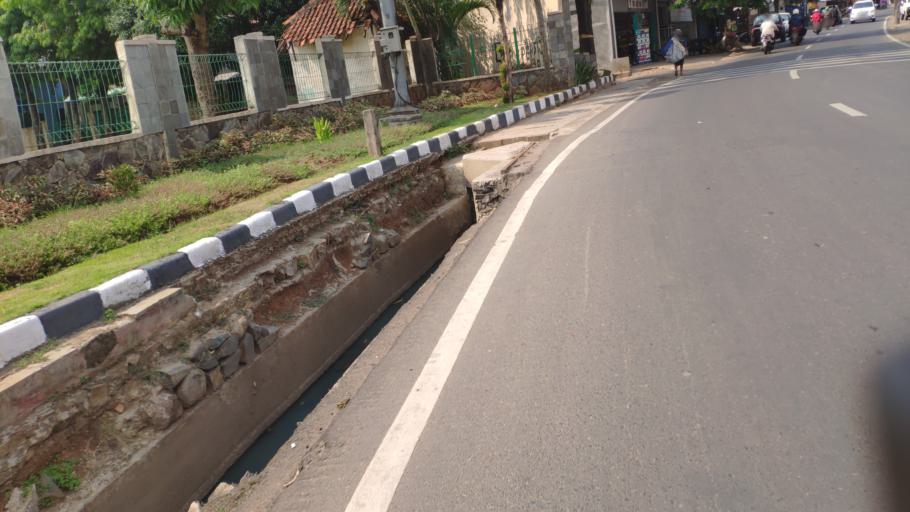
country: ID
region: West Java
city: Pamulang
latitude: -6.3198
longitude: 106.8107
